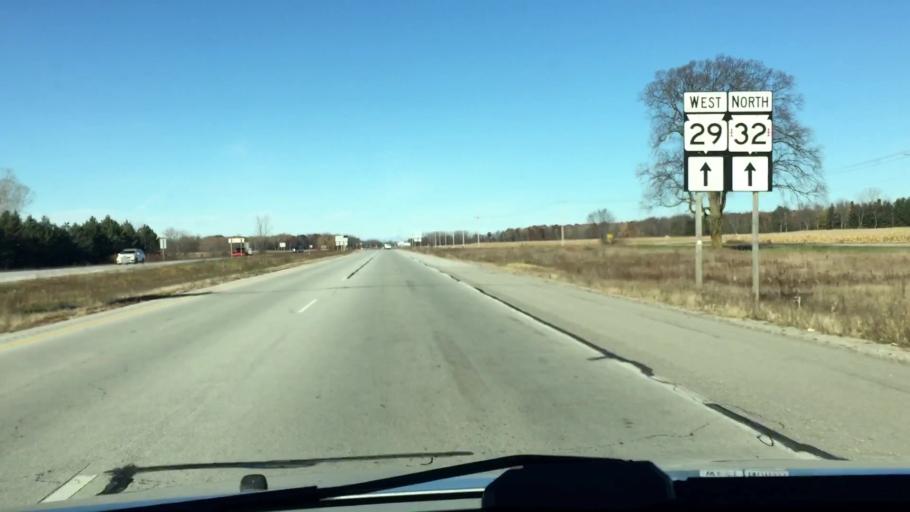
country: US
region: Wisconsin
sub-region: Brown County
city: Oneida
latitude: 44.5752
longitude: -88.1675
